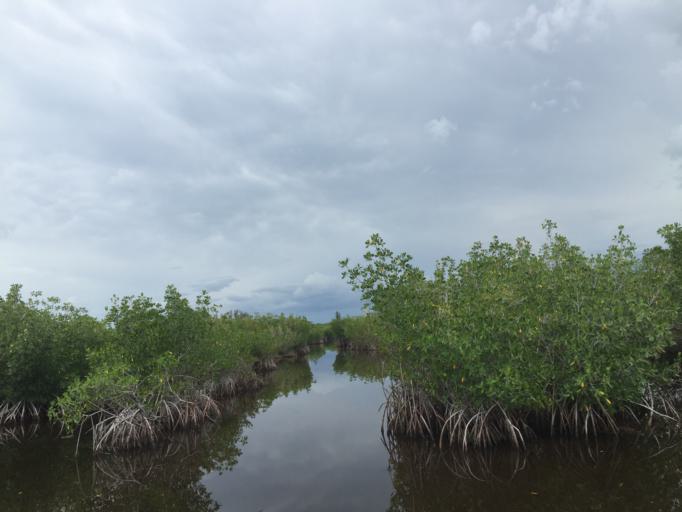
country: US
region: Florida
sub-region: Collier County
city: Marco
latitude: 25.9066
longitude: -81.3710
